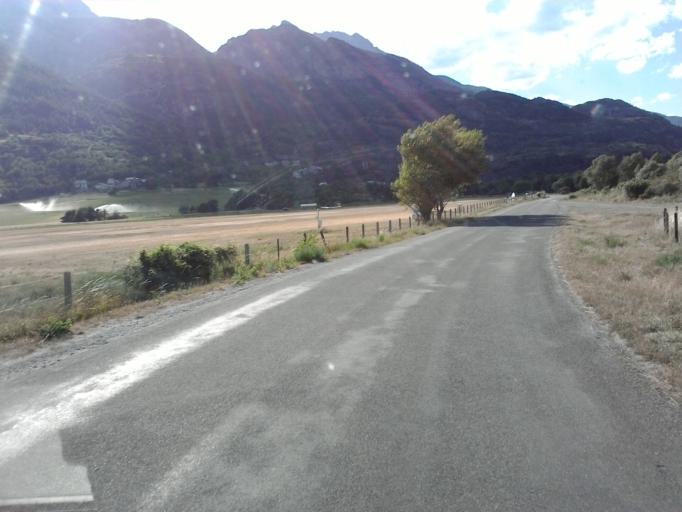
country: FR
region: Provence-Alpes-Cote d'Azur
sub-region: Departement des Hautes-Alpes
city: Guillestre
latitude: 44.7048
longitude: 6.5999
